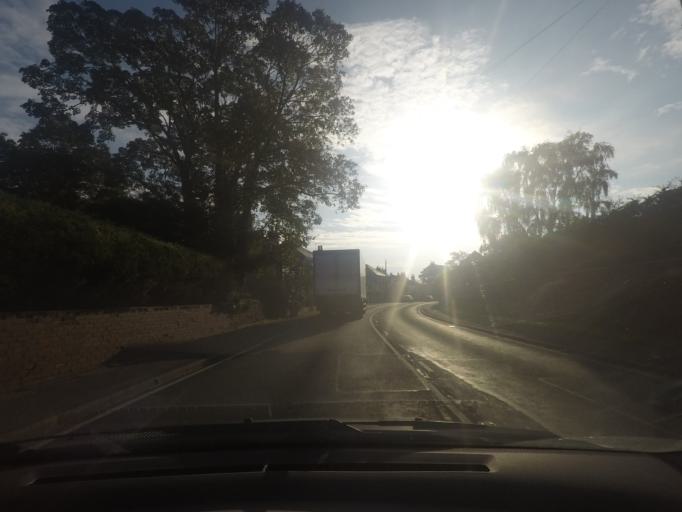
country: GB
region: England
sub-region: East Riding of Yorkshire
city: Londesborough
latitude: 53.8785
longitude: -0.7070
